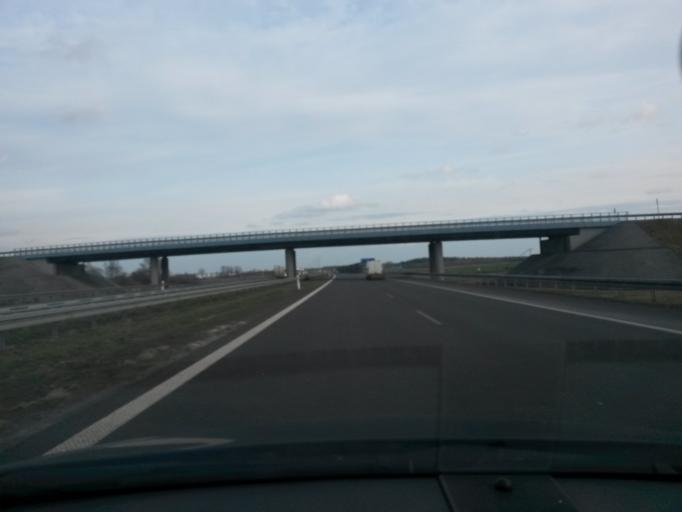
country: PL
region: Greater Poland Voivodeship
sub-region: Powiat kolski
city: Dabie
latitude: 52.0750
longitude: 18.8066
